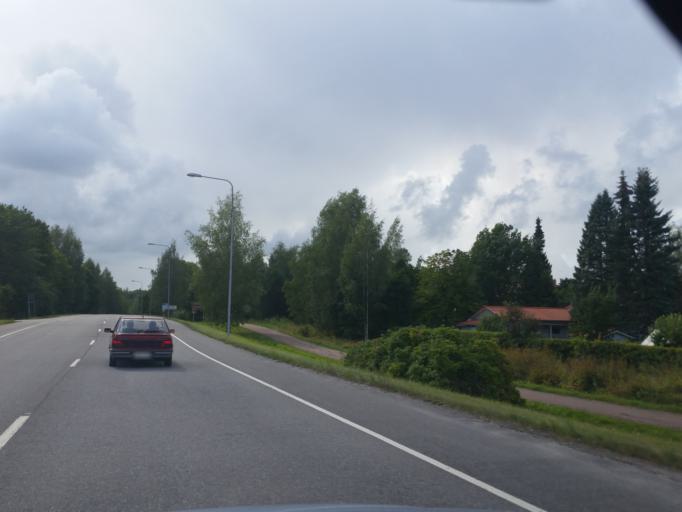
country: FI
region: Varsinais-Suomi
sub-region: Aboland-Turunmaa
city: Pargas
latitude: 60.3055
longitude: 22.2981
